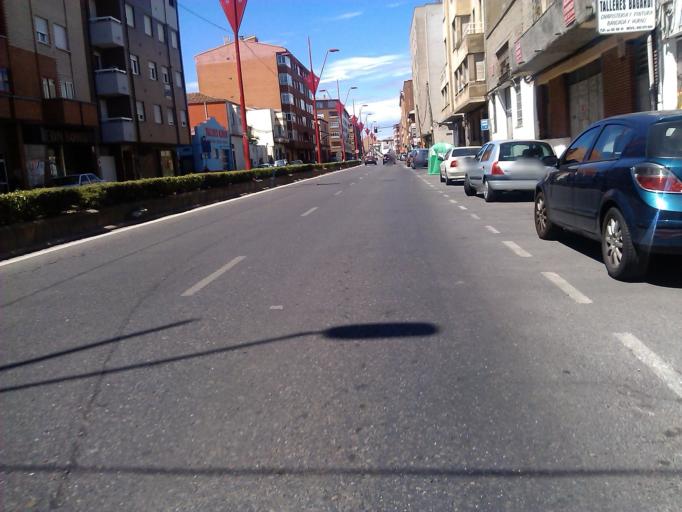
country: ES
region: Castille and Leon
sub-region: Provincia de Leon
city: Leon
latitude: 42.5985
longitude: -5.5948
